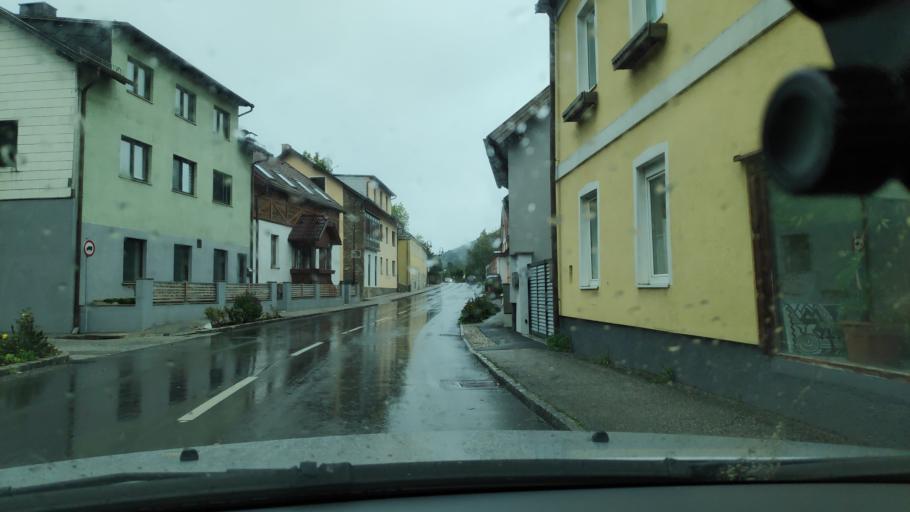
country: AT
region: Lower Austria
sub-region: Politischer Bezirk Neunkirchen
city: Grunbach am Schneeberg
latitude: 47.7963
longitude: 15.9893
